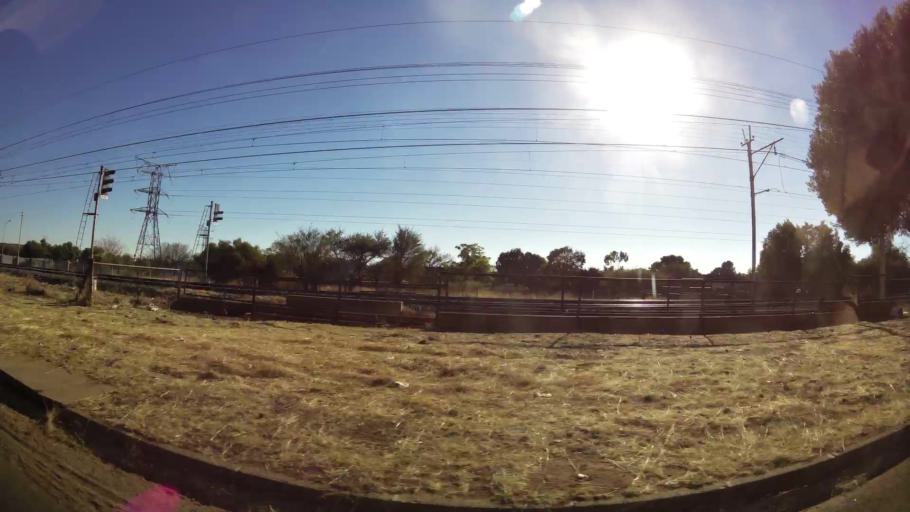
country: ZA
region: Northern Cape
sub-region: Frances Baard District Municipality
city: Kimberley
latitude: -28.7442
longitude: 24.7825
